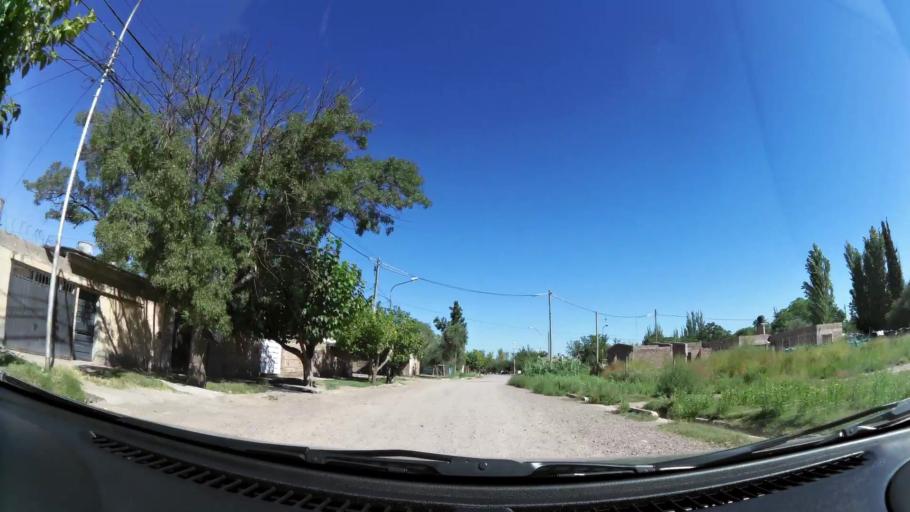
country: AR
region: Mendoza
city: Las Heras
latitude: -32.8271
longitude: -68.8223
